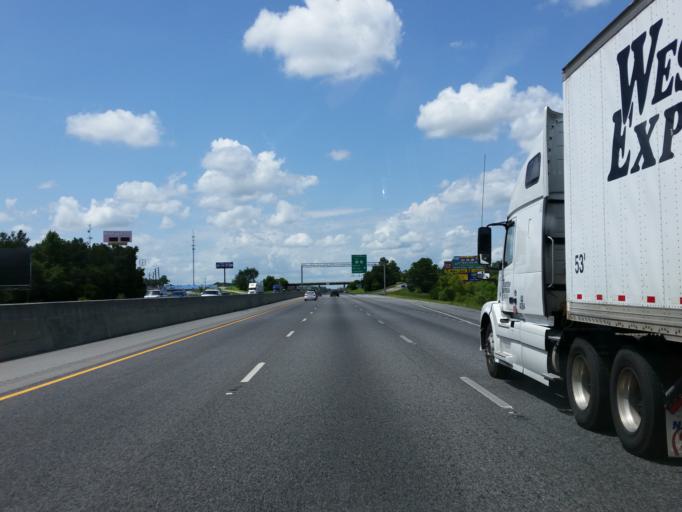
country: US
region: Georgia
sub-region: Lowndes County
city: Hahira
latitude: 30.9877
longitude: -83.3866
